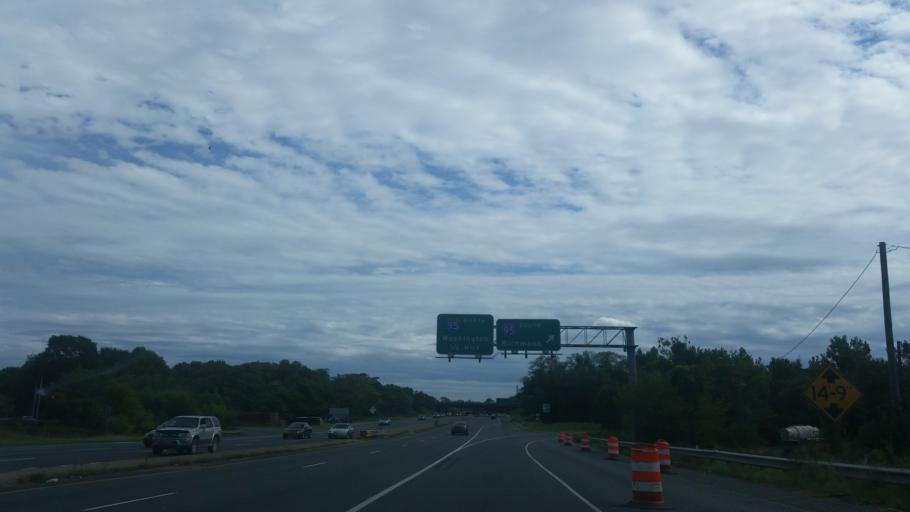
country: US
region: Virginia
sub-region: Stafford County
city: Falmouth
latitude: 38.3427
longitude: -77.4957
